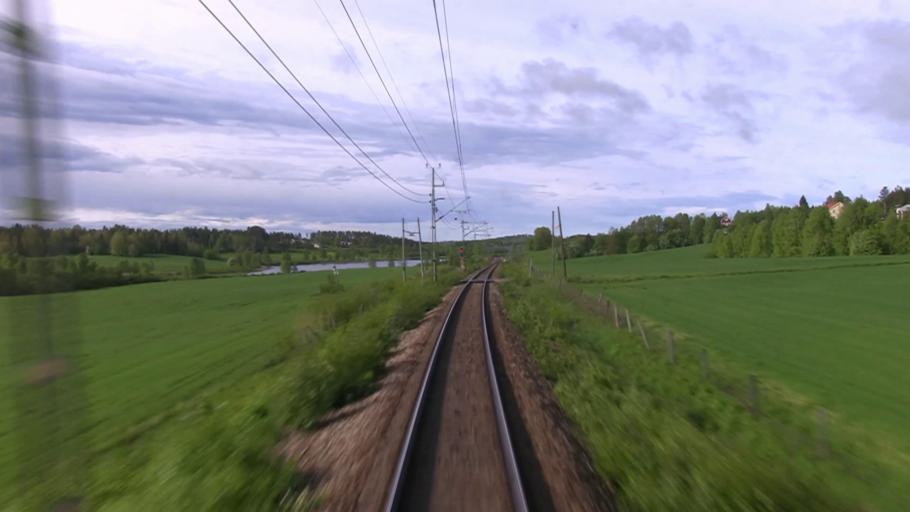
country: SE
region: Vaesterbotten
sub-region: Vindelns Kommun
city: Vindeln
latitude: 64.1050
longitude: 19.6834
